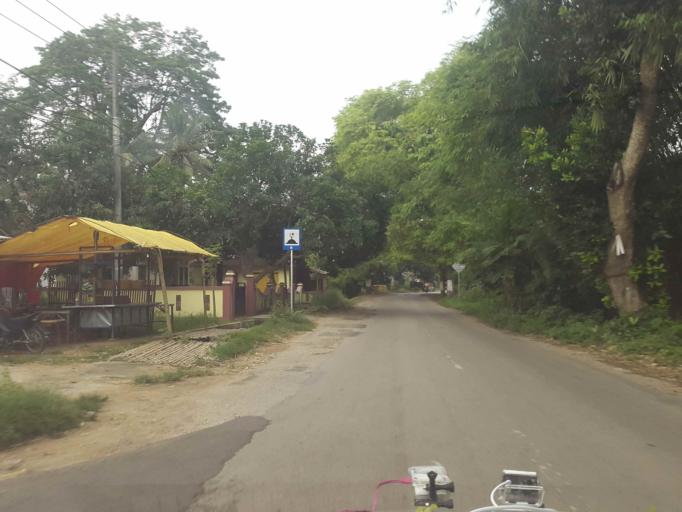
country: ID
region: East Java
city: Ganjur
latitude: -6.9834
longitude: 113.8595
